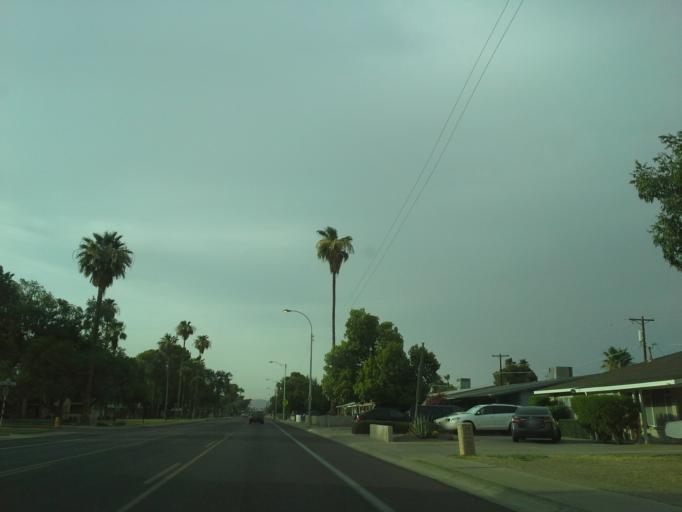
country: US
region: Arizona
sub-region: Maricopa County
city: Phoenix
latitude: 33.5036
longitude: -112.0912
